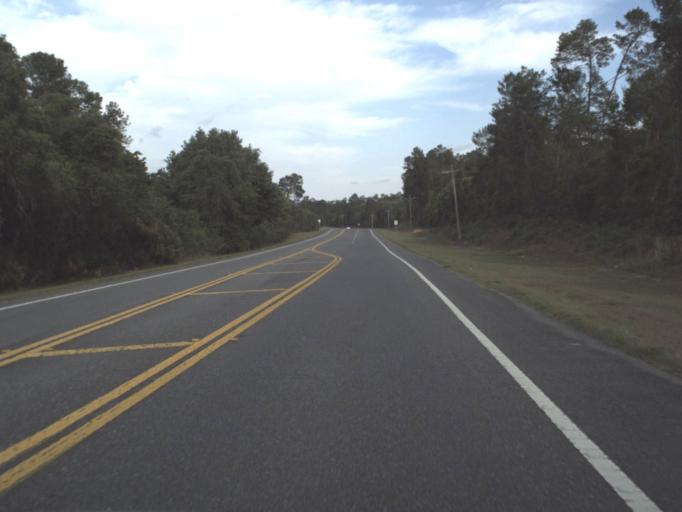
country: US
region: Florida
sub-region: Lake County
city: Astor
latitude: 29.1753
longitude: -81.6969
